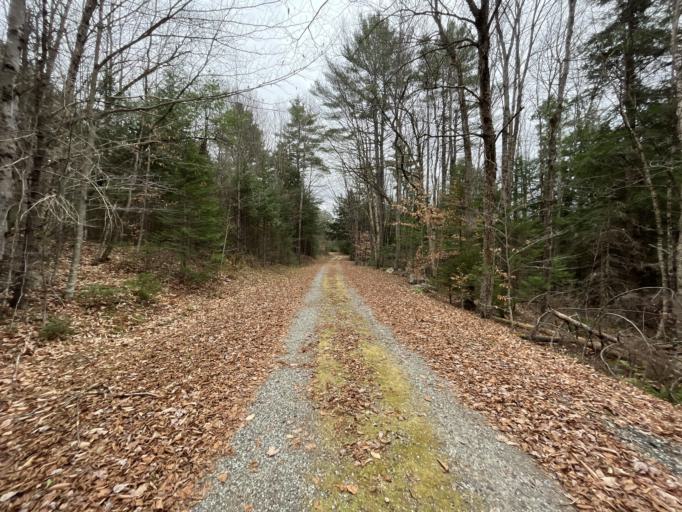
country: US
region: New Hampshire
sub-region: Merrimack County
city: New London
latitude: 43.4063
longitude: -71.9838
